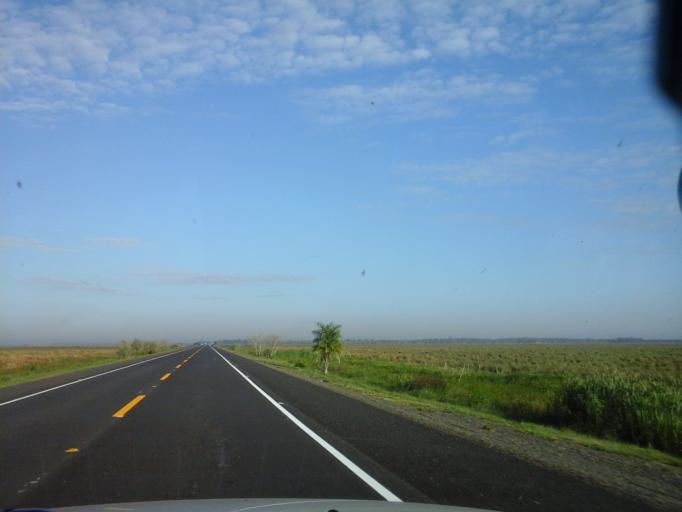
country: PY
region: Neembucu
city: Cerrito
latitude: -26.8681
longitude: -57.7772
